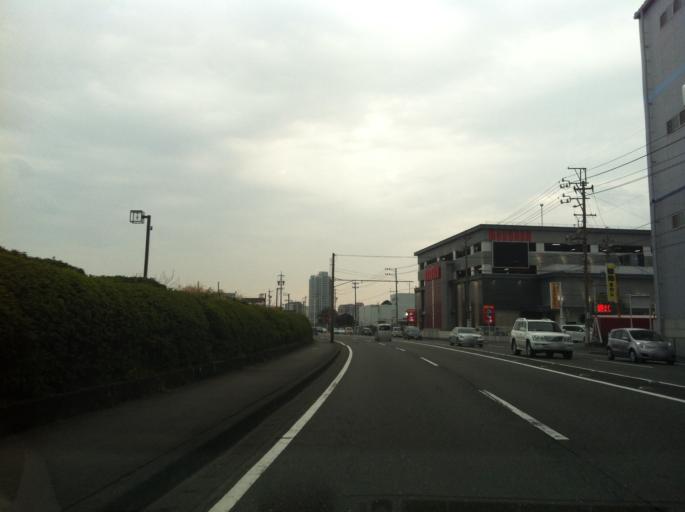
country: JP
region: Shizuoka
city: Shizuoka-shi
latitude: 35.0325
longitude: 138.4945
